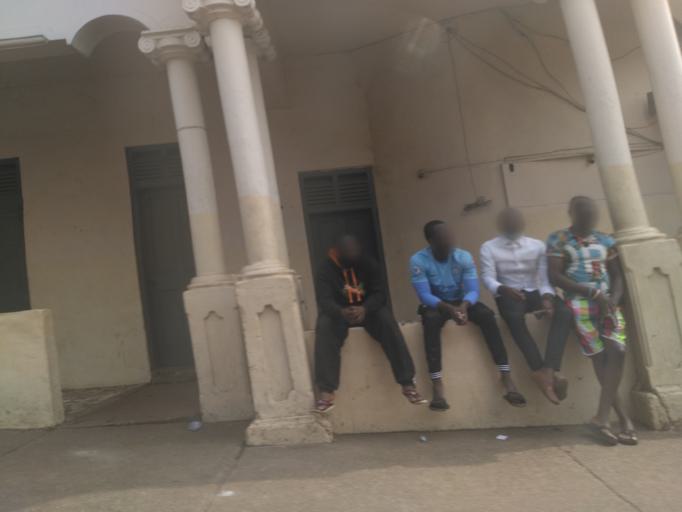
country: GH
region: Ashanti
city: Kumasi
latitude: 6.7042
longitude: -1.6193
